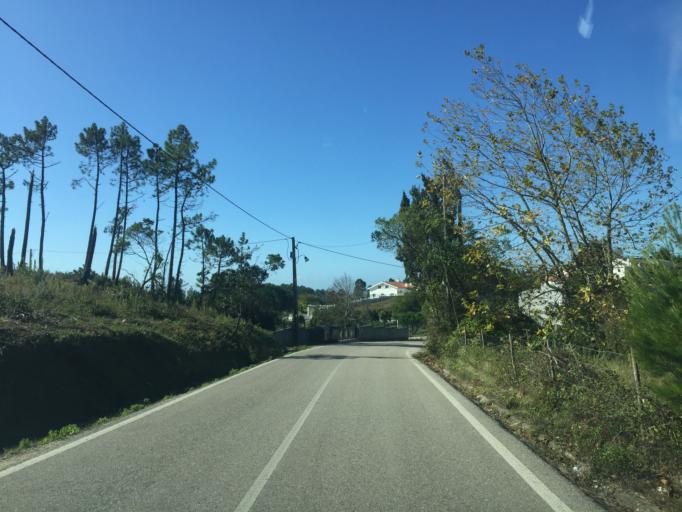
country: PT
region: Coimbra
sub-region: Figueira da Foz
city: Tavarede
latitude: 40.1882
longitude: -8.8344
